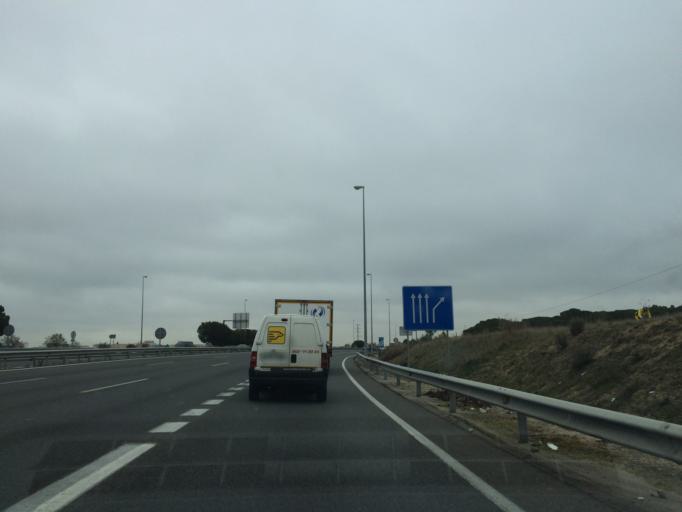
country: ES
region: Madrid
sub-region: Provincia de Madrid
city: Tres Cantos
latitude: 40.5960
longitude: -3.7158
